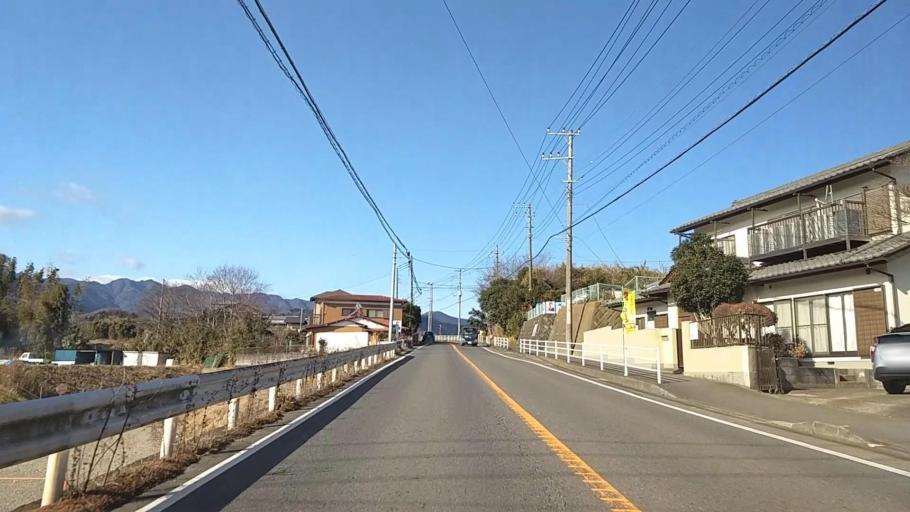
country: JP
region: Kanagawa
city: Atsugi
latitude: 35.4682
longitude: 139.3323
